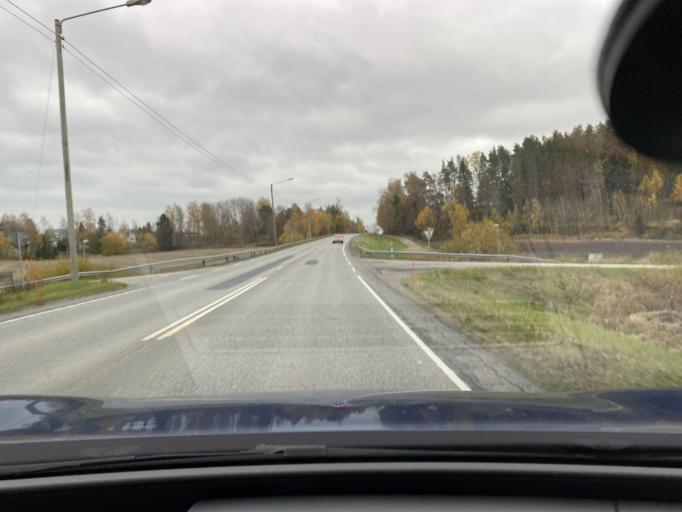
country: FI
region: Varsinais-Suomi
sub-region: Vakka-Suomi
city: Pyhaeranta
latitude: 60.9882
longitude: 21.5848
